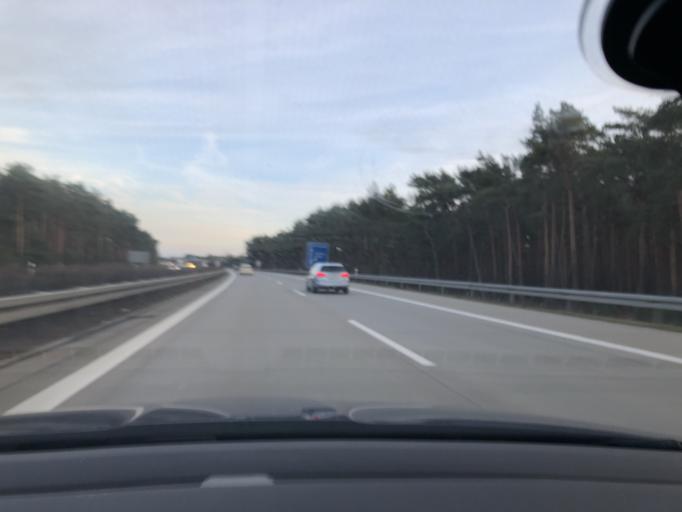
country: DE
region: Brandenburg
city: Kasel-Golzig
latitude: 52.0191
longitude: 13.6895
